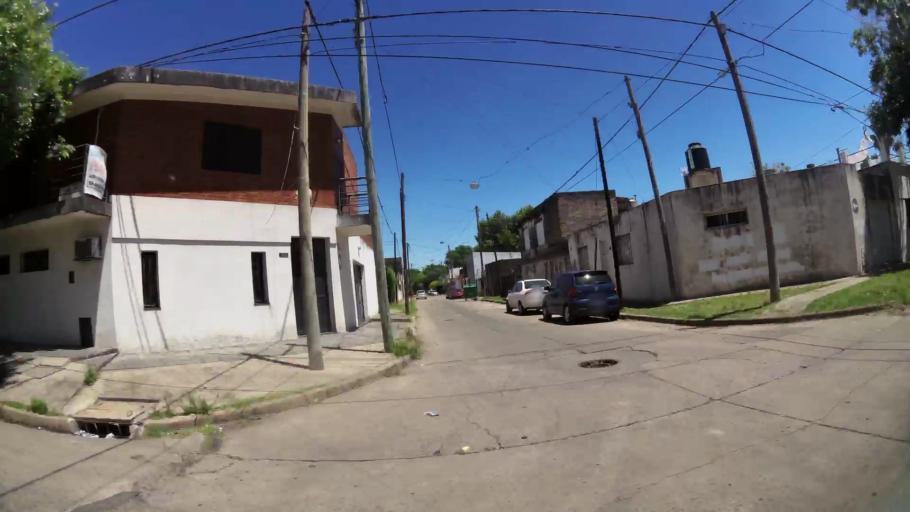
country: AR
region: Santa Fe
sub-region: Departamento de Rosario
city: Rosario
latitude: -32.9449
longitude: -60.7021
